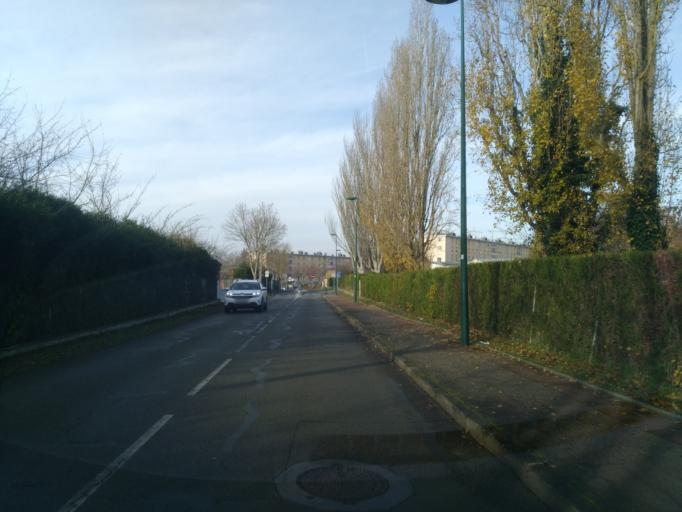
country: FR
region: Ile-de-France
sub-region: Departement des Yvelines
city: Plaisir
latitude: 48.8253
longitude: 1.9479
